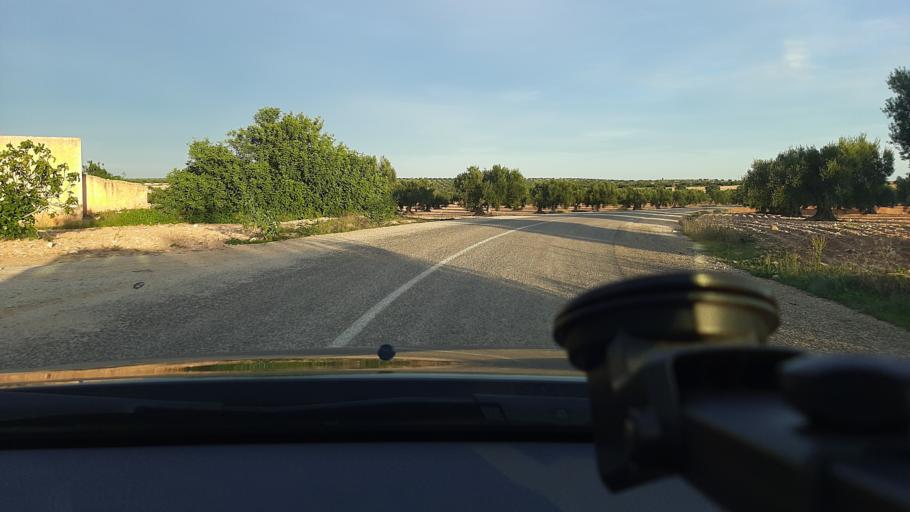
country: TN
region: Safaqis
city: Sfax
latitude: 34.9574
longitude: 10.5412
